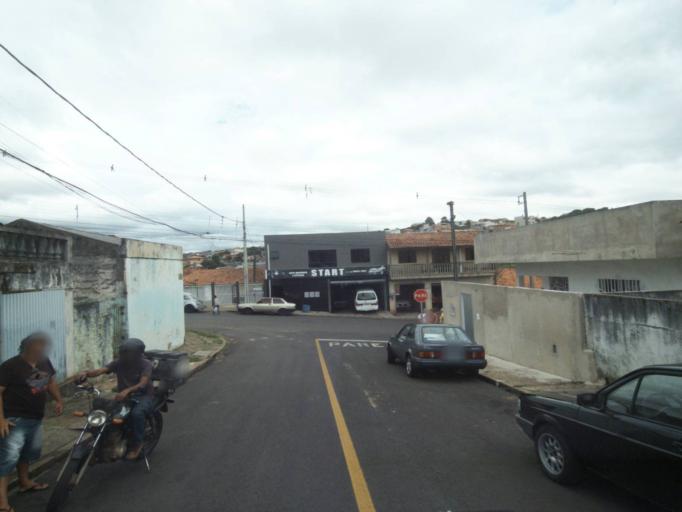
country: BR
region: Parana
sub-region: Telemaco Borba
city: Telemaco Borba
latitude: -24.3267
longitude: -50.6294
